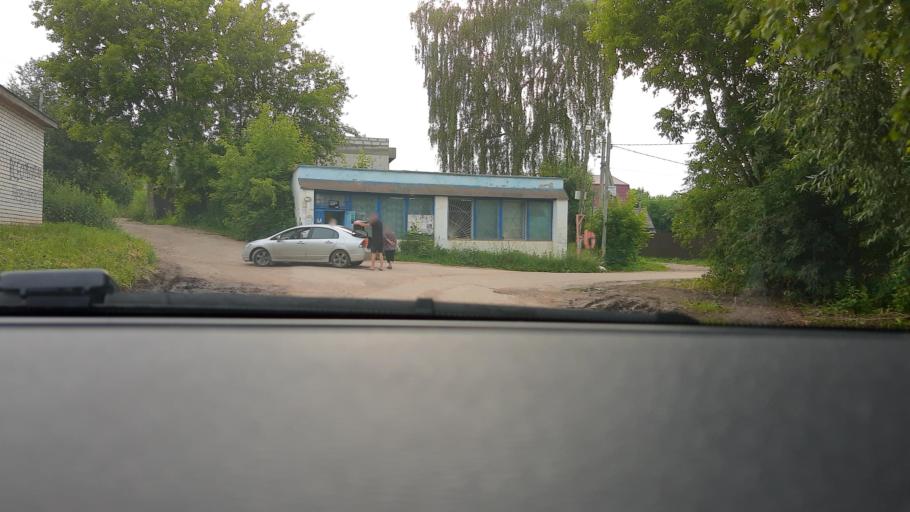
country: RU
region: Nizjnij Novgorod
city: Afonino
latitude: 56.2518
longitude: 44.0765
